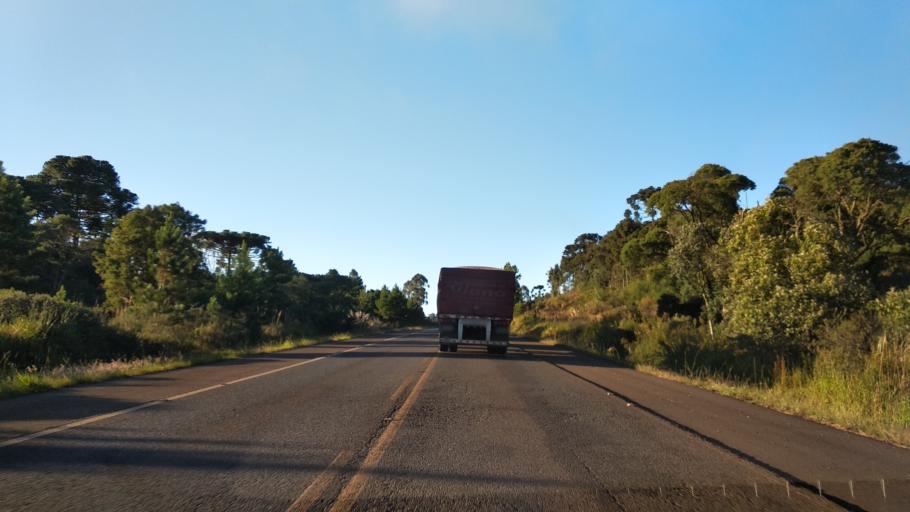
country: BR
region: Santa Catarina
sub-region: Correia Pinto
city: Correia Pinto
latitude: -27.6388
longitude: -50.5979
